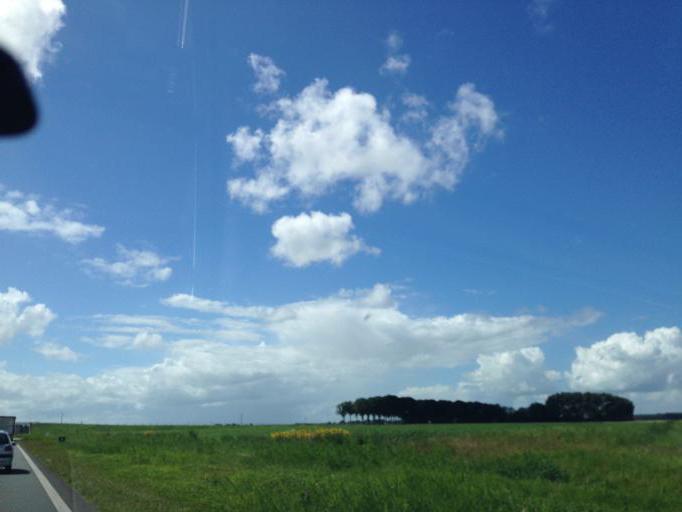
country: NL
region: Flevoland
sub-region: Gemeente Dronten
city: Dronten
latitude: 52.5487
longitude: 5.6760
